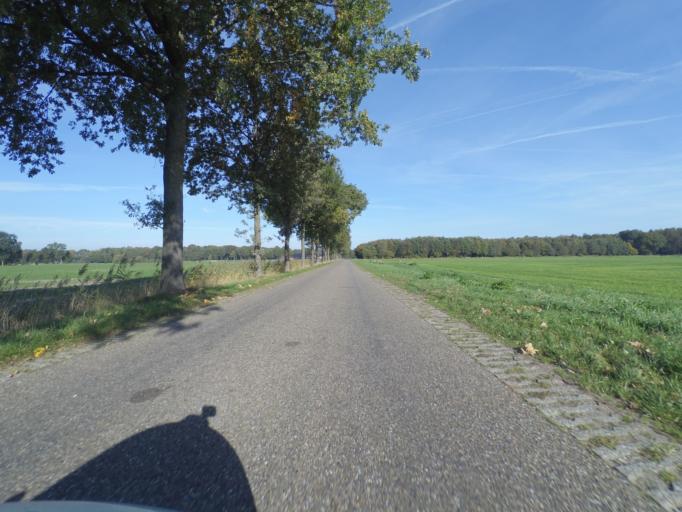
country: NL
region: Gelderland
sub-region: Berkelland
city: Borculo
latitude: 52.0774
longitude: 6.5124
